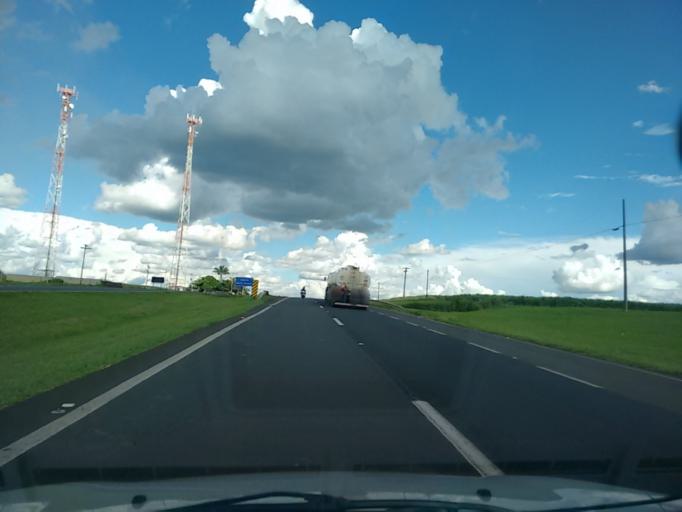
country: BR
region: Sao Paulo
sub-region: Ibate
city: Ibate
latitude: -21.9124
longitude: -48.0458
